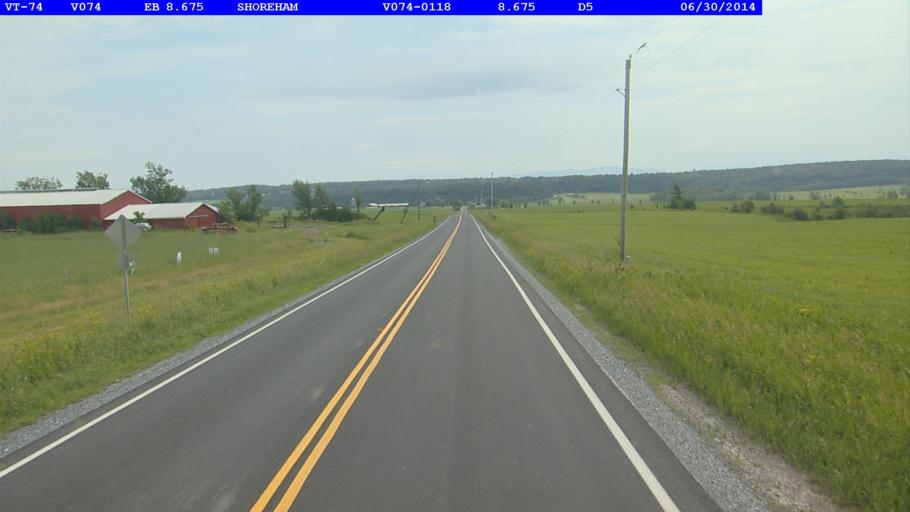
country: US
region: Vermont
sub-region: Addison County
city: Middlebury (village)
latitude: 43.9413
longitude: -73.2808
